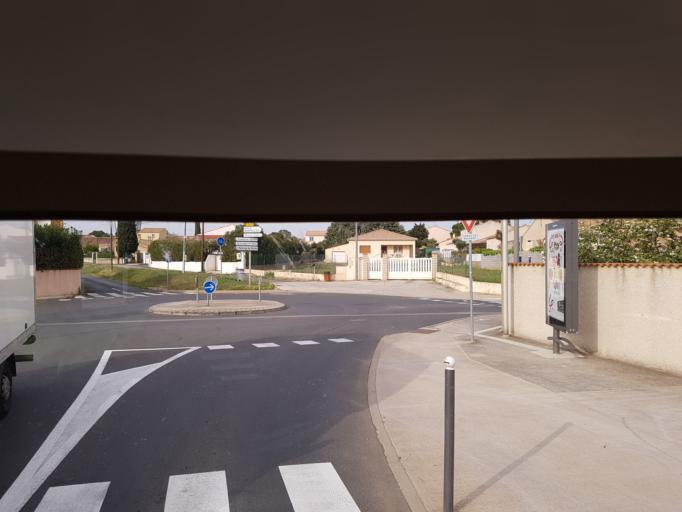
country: FR
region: Languedoc-Roussillon
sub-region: Departement de l'Herault
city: Marseillan
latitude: 43.3603
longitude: 3.5245
